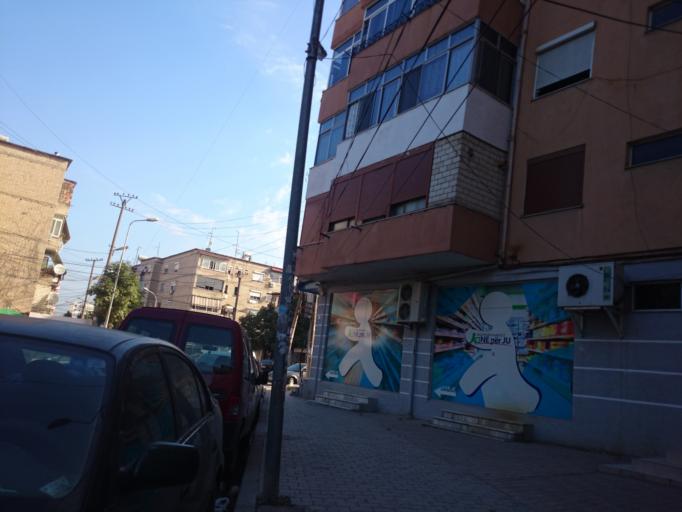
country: AL
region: Tirane
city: Tirana
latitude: 41.3189
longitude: 19.7994
